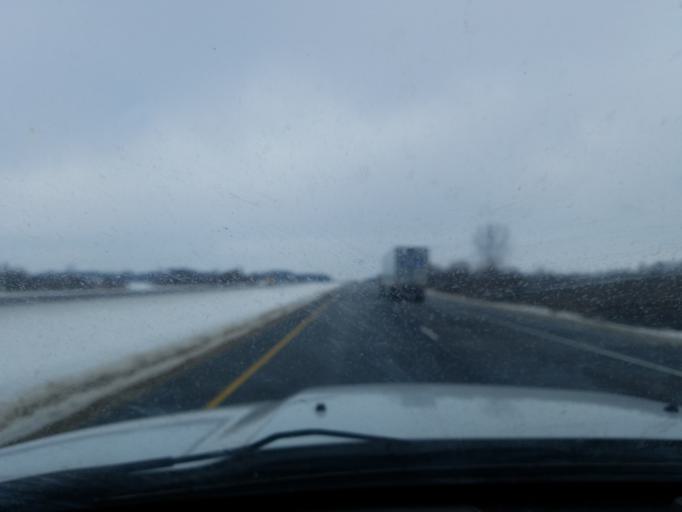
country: US
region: Indiana
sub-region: Marshall County
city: Argos
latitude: 41.2600
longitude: -86.2641
